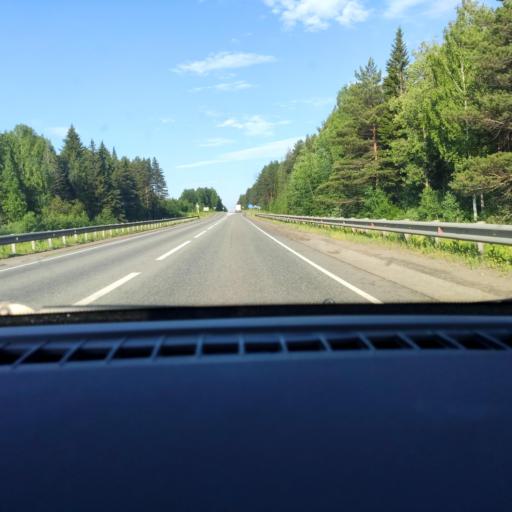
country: RU
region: Udmurtiya
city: Khokhryaki
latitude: 56.9513
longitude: 53.6366
